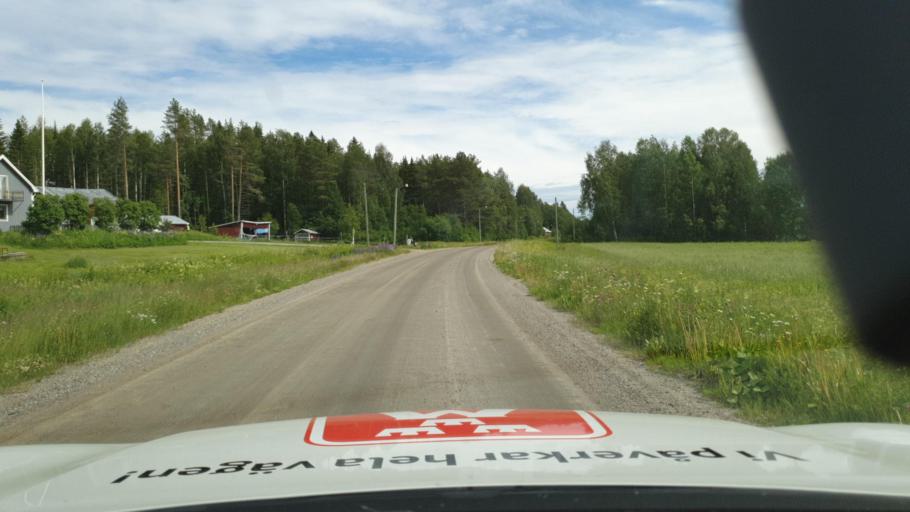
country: SE
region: Vaesterbotten
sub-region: Skelleftea Kommun
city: Burtraesk
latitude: 64.4925
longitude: 20.5959
